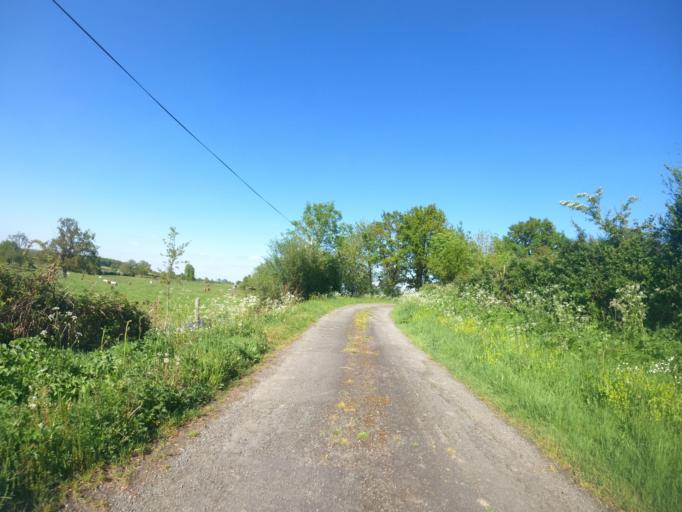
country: FR
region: Poitou-Charentes
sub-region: Departement des Deux-Sevres
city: Moncoutant
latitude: 46.6804
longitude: -0.5330
